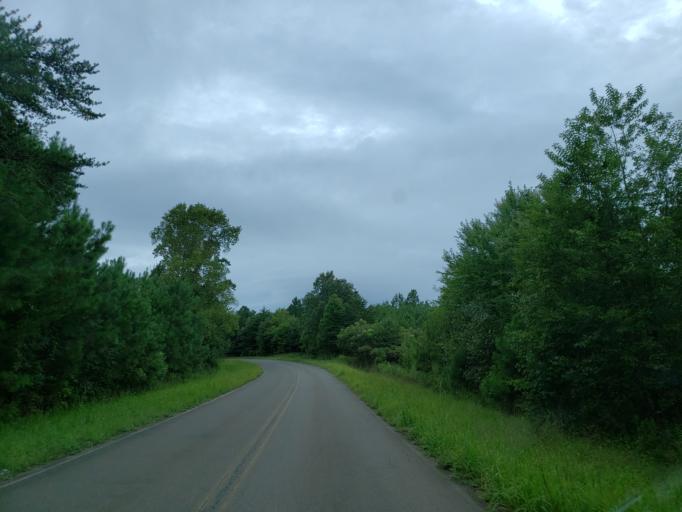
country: US
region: Georgia
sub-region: Pickens County
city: Jasper
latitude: 34.4242
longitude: -84.5749
